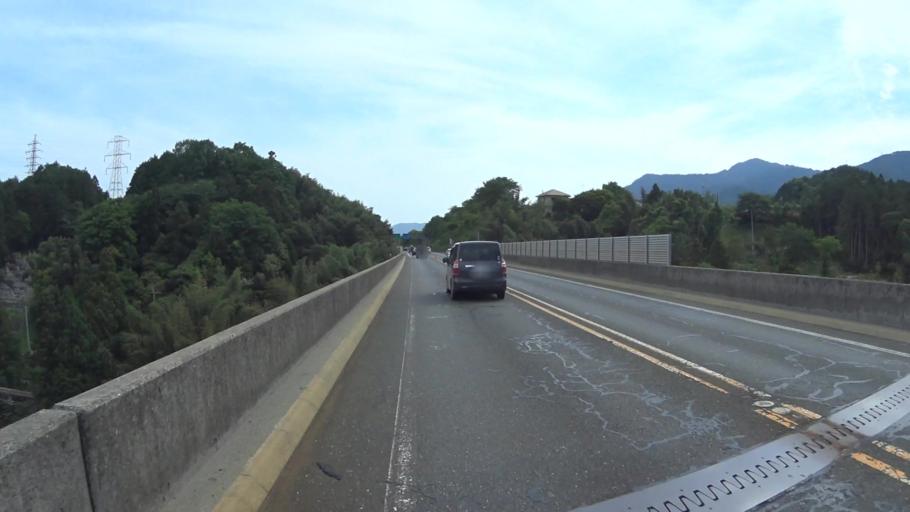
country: JP
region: Shiga Prefecture
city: Otsu-shi
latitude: 35.0858
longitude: 135.8851
